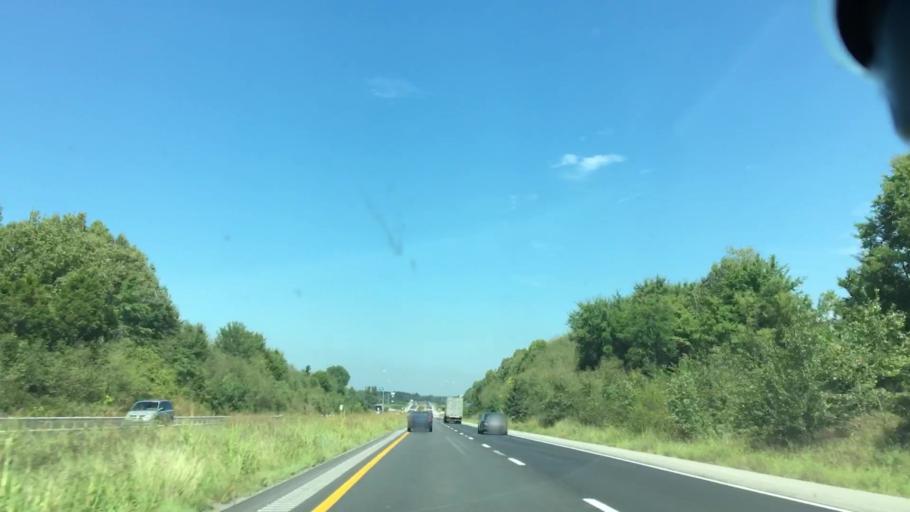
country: US
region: Kentucky
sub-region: Hopkins County
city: Madisonville
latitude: 37.4059
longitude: -87.4744
